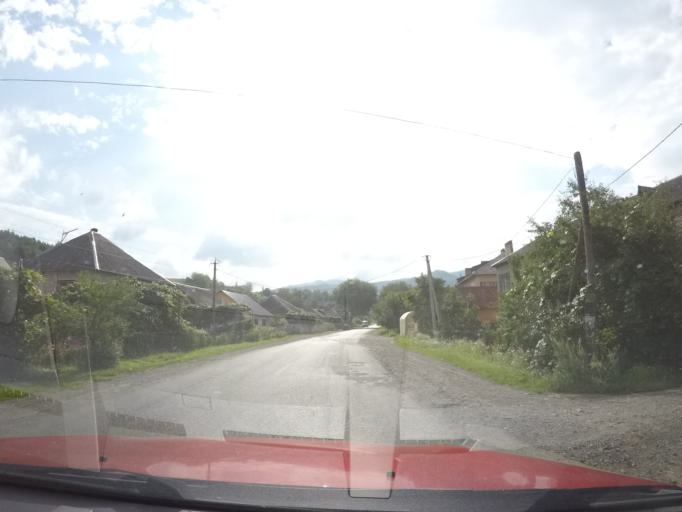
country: UA
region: Zakarpattia
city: Velykyi Bereznyi
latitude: 48.9421
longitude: 22.5842
